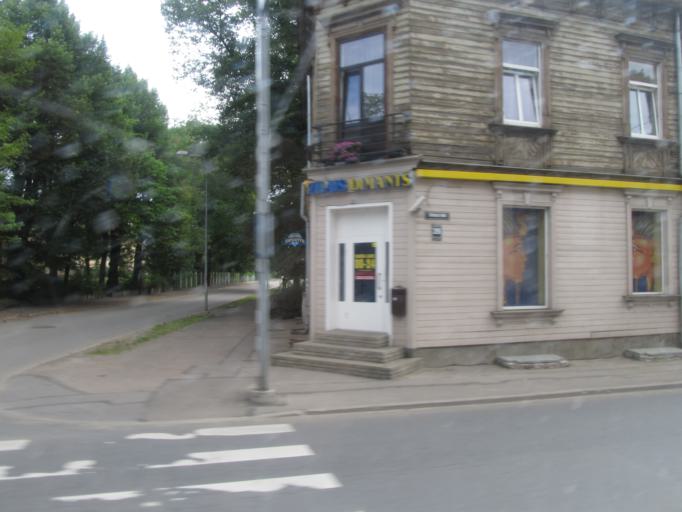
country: LV
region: Riga
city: Riga
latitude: 56.9484
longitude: 24.0723
